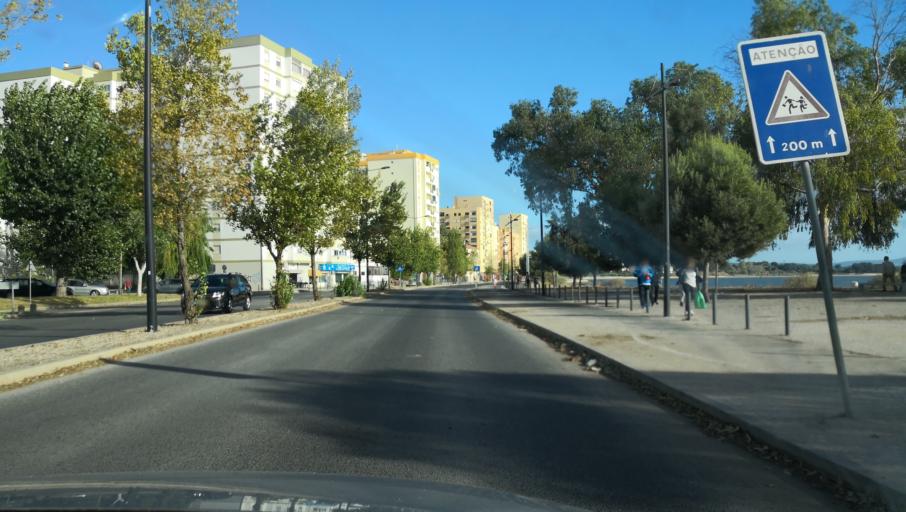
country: PT
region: Setubal
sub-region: Barreiro
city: Barreiro
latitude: 38.6533
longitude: -9.0743
